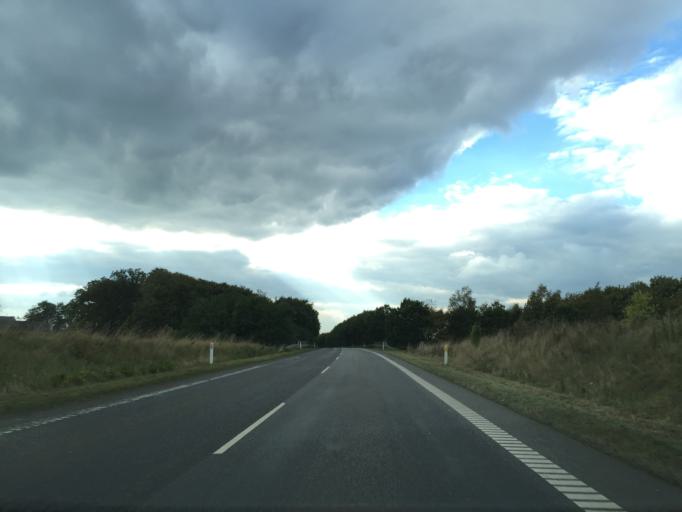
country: DK
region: Central Jutland
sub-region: Favrskov Kommune
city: Ulstrup
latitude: 56.3181
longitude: 9.7865
